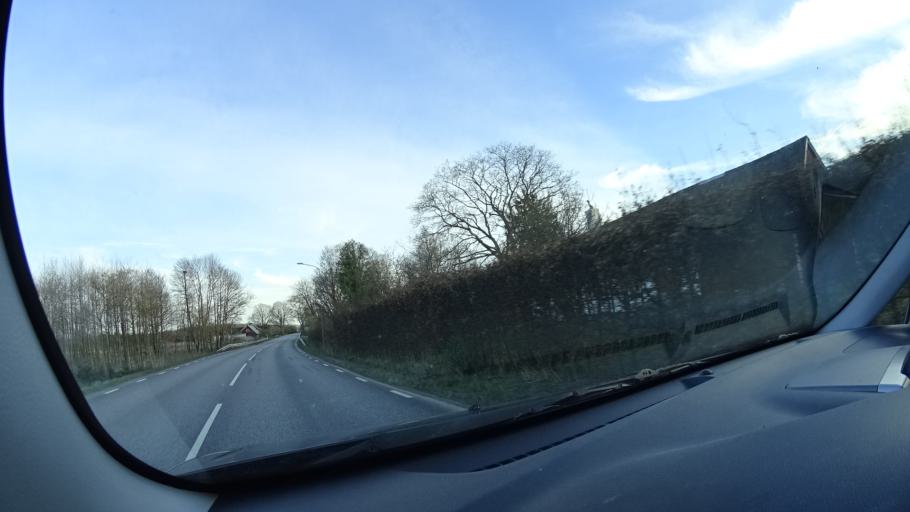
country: SE
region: Skane
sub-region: Eslovs Kommun
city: Stehag
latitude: 55.9745
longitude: 13.3284
